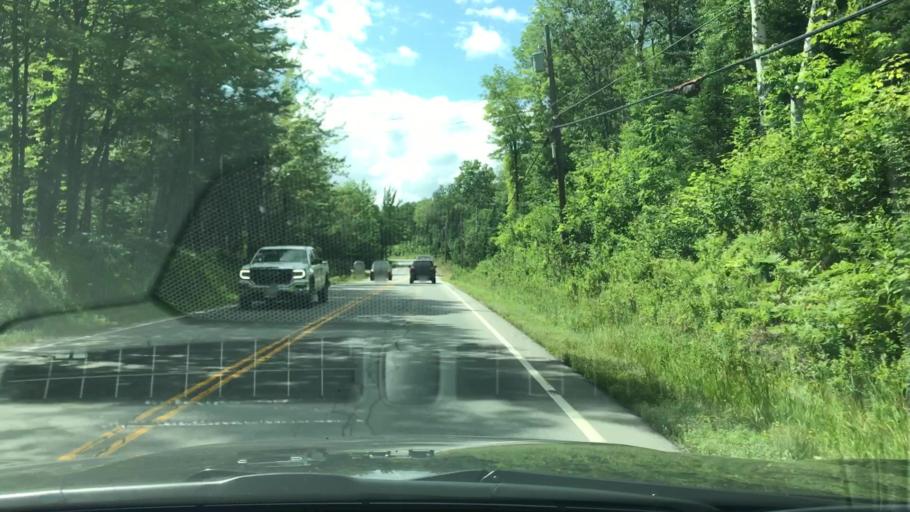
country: US
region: New Hampshire
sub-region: Coos County
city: Jefferson
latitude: 44.3611
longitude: -71.3765
